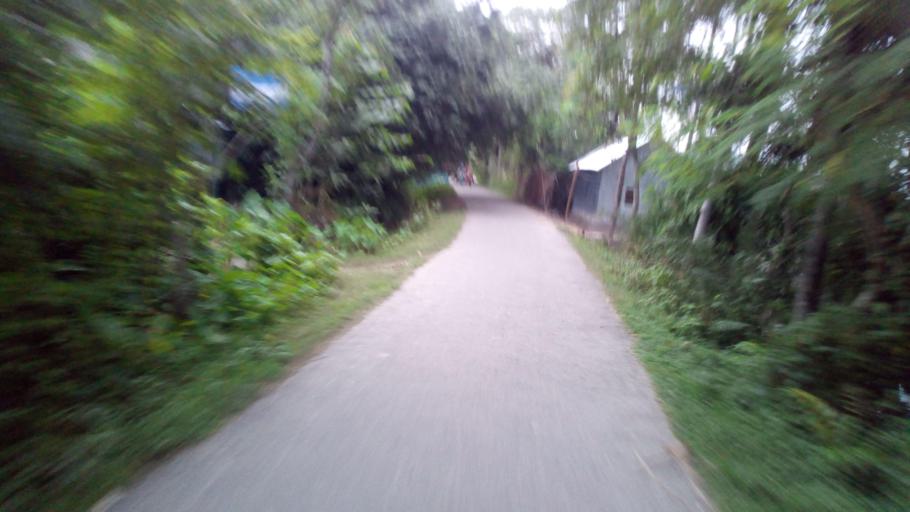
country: BD
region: Khulna
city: Phultala
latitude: 22.7603
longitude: 89.4080
